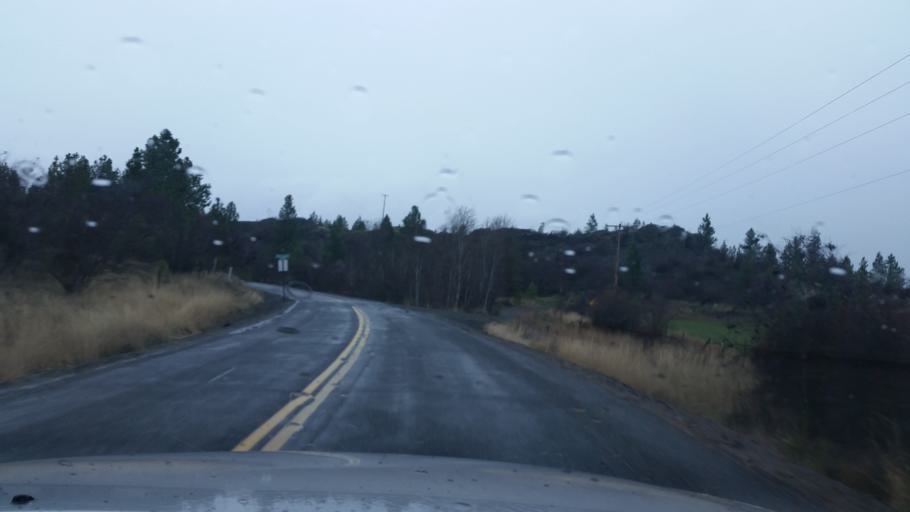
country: US
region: Washington
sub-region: Spokane County
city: Airway Heights
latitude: 47.6967
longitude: -117.5719
